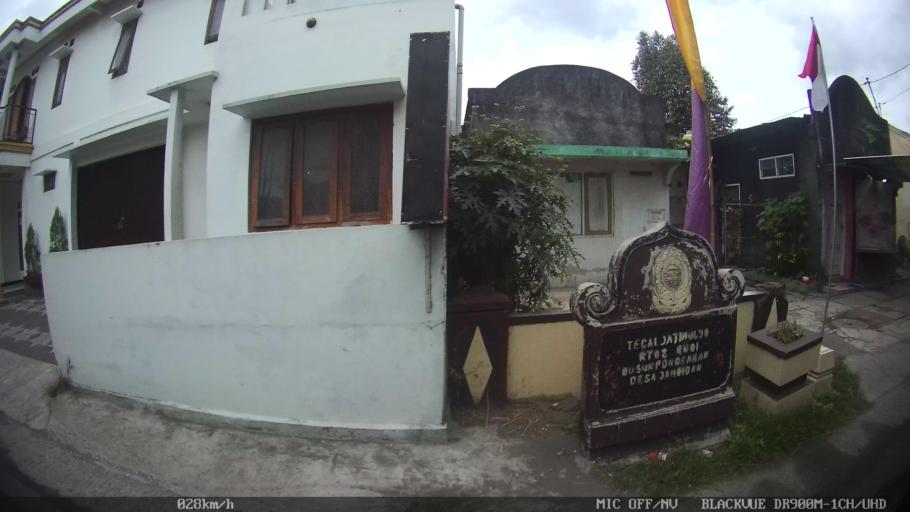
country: ID
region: Daerah Istimewa Yogyakarta
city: Sewon
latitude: -7.8585
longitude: 110.4093
